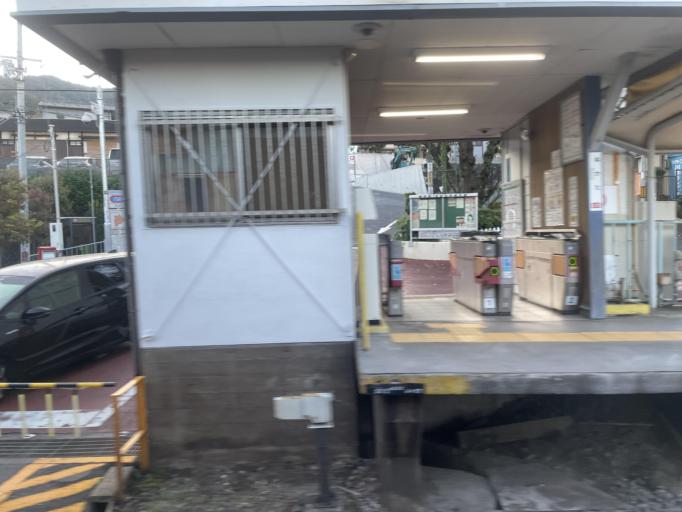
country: JP
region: Osaka
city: Daitocho
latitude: 34.6757
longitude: 135.6513
